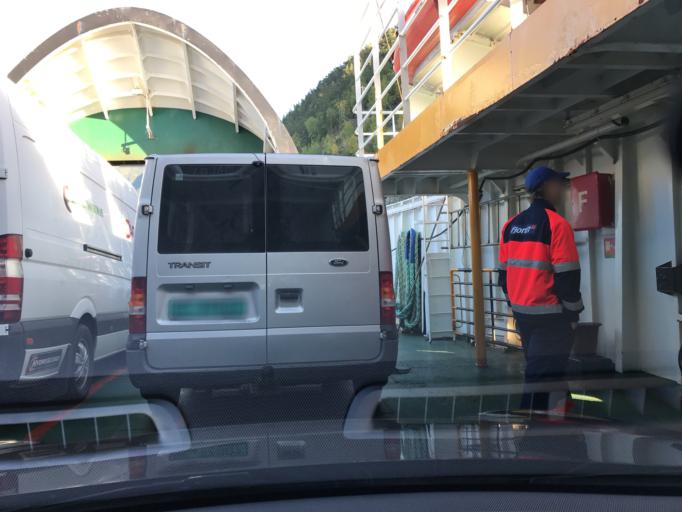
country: NO
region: Sogn og Fjordane
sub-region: Laerdal
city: Laerdalsoyri
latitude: 61.1486
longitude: 7.3812
